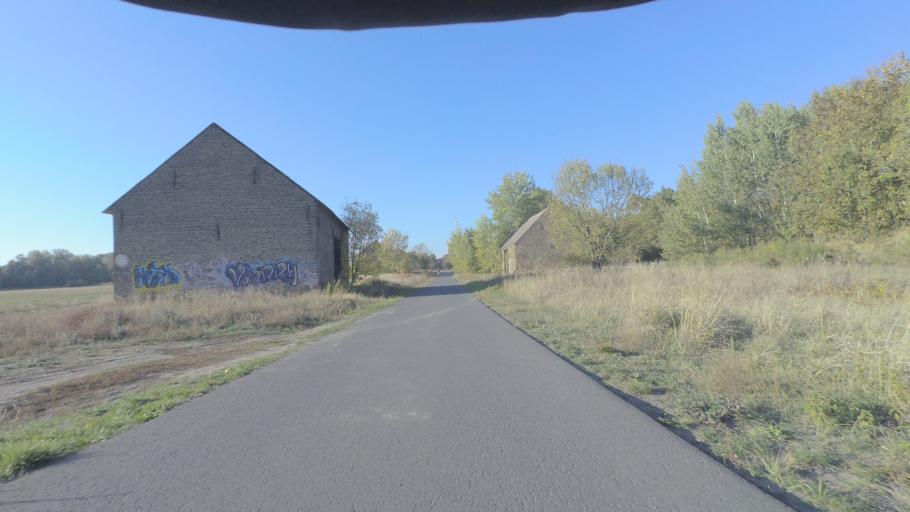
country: DE
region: Brandenburg
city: Mittenwalde
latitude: 52.2564
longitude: 13.5413
